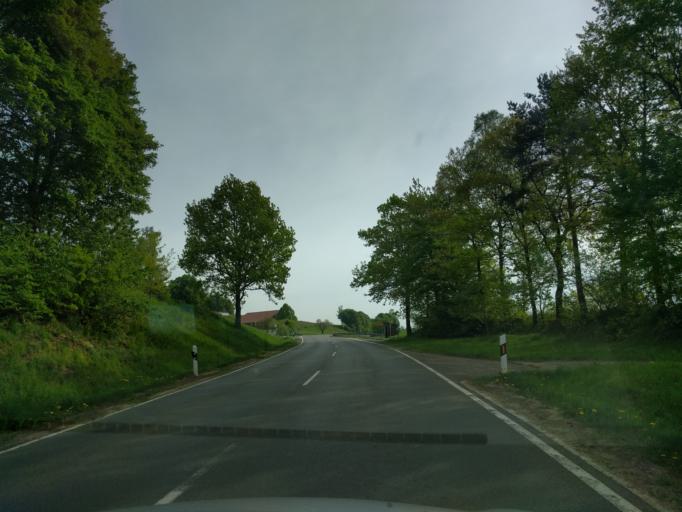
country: DE
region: Bavaria
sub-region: Upper Palatinate
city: Michelsneukirchen
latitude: 49.1170
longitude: 12.5264
